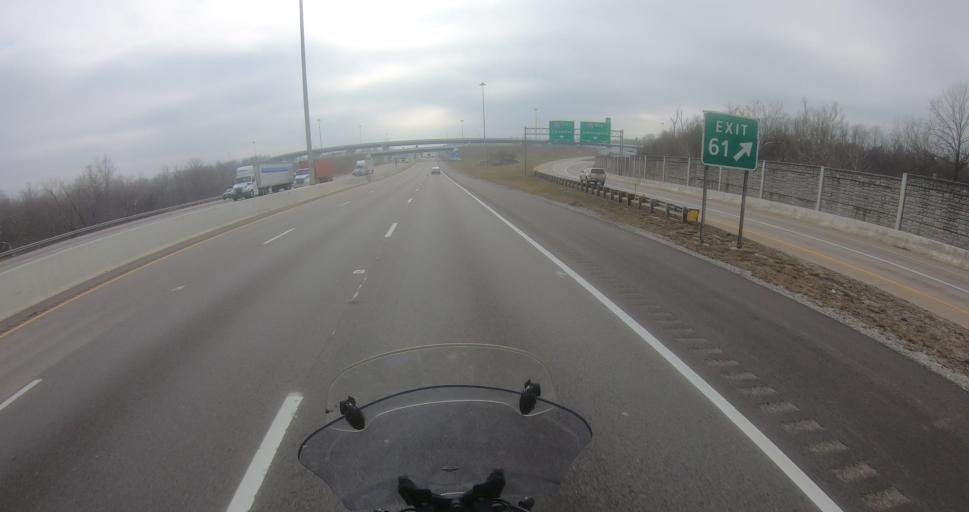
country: US
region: Ohio
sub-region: Montgomery County
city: Vandalia
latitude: 39.8699
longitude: -84.1887
